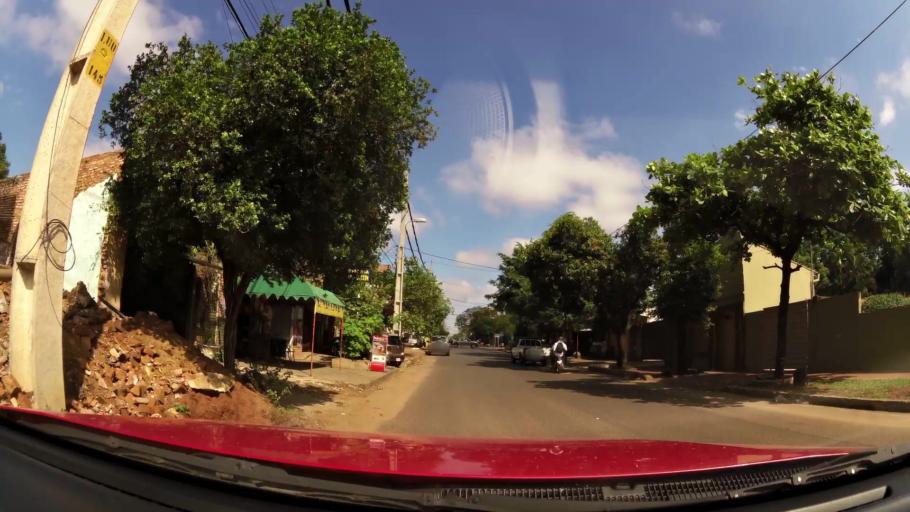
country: PY
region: Central
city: San Lorenzo
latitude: -25.2643
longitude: -57.4893
